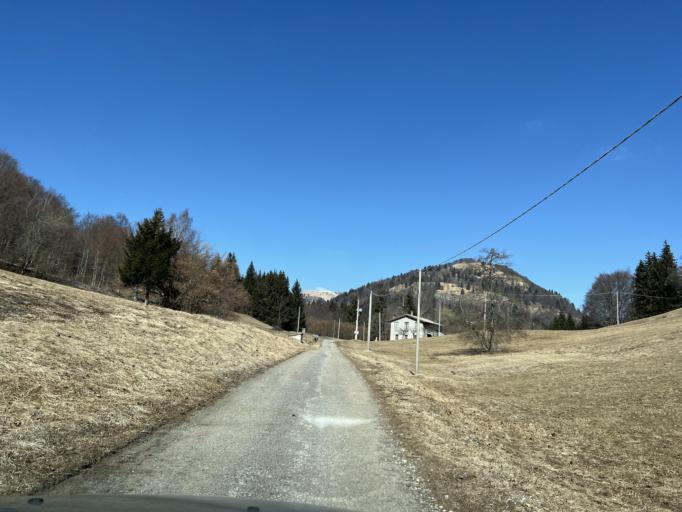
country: IT
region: Friuli Venezia Giulia
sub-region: Provincia di Udine
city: Chiaulis
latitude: 46.4206
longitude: 12.9775
